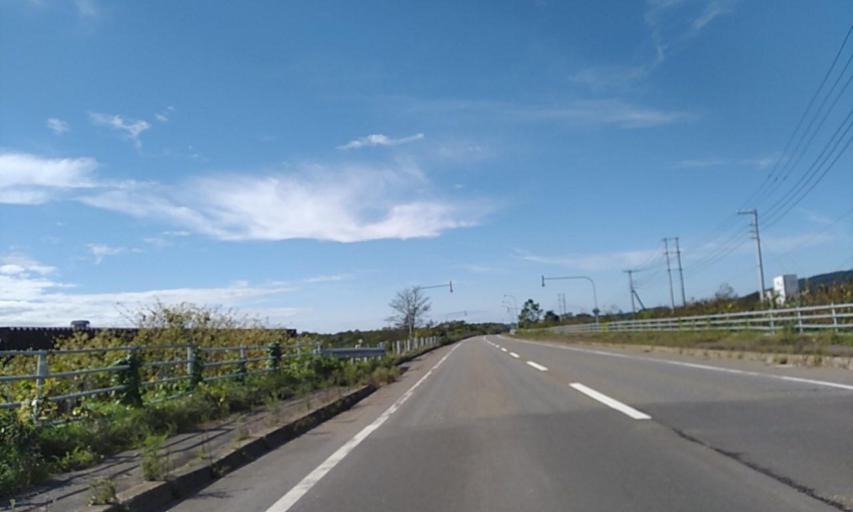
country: JP
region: Hokkaido
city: Obihiro
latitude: 42.7797
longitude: 143.6013
